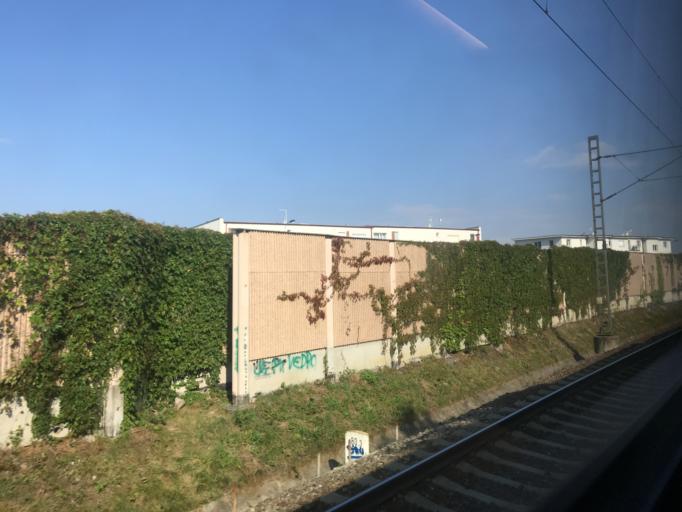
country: CZ
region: Jihocesky
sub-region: Okres Tabor
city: Sezimovo Usti
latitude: 49.4014
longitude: 14.6839
